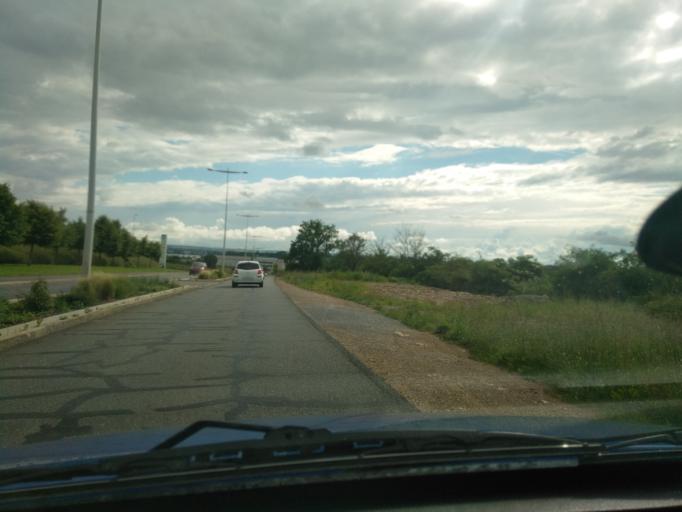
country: FR
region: Midi-Pyrenees
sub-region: Departement de l'Aveyron
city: Sebazac-Concoures
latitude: 44.3933
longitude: 2.6007
